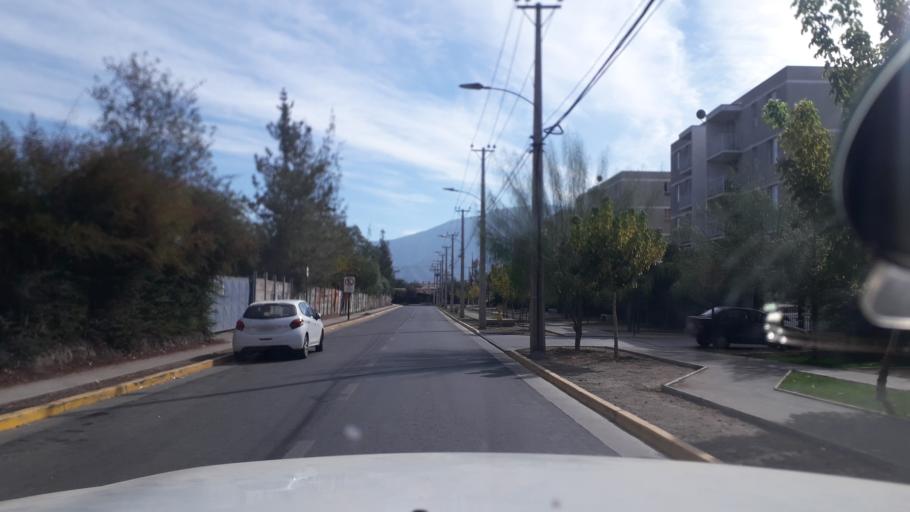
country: CL
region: Valparaiso
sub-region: Provincia de San Felipe
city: San Felipe
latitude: -32.7471
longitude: -70.7322
